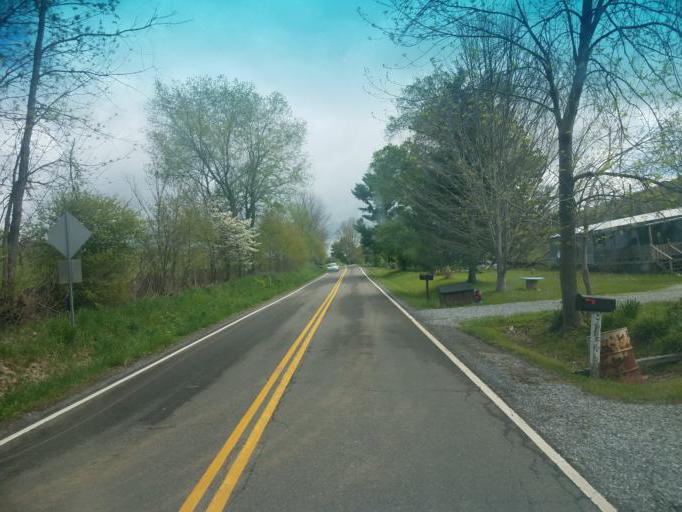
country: US
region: Virginia
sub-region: Wythe County
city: Rural Retreat
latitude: 37.0089
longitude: -81.3599
